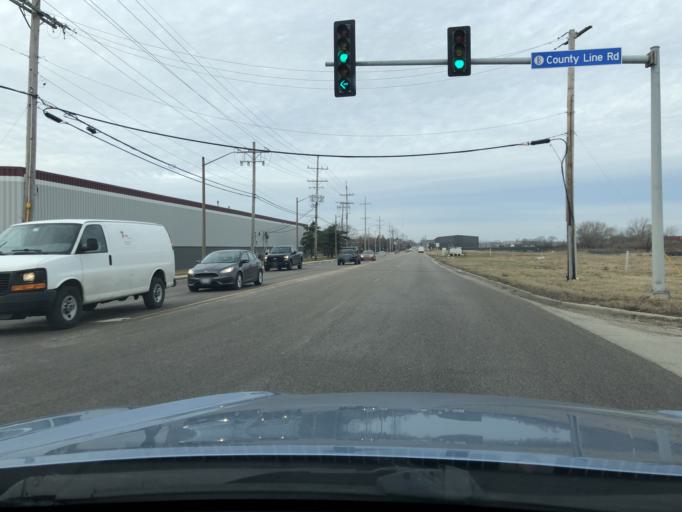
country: US
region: Illinois
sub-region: DuPage County
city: Bensenville
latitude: 41.9495
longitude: -87.9202
